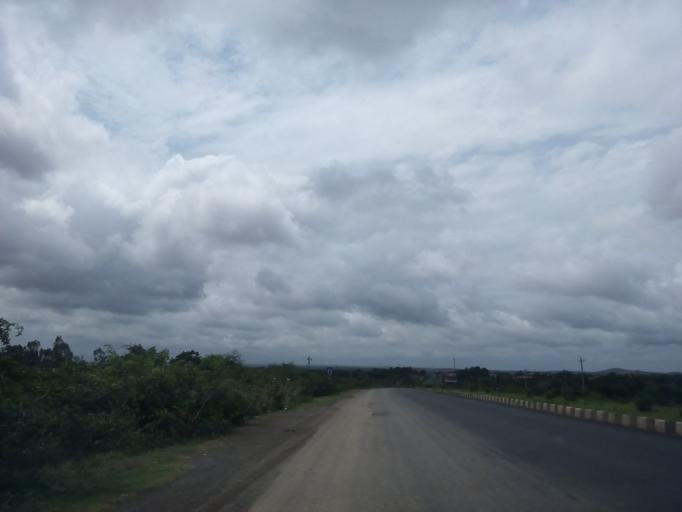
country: IN
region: Karnataka
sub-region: Haveri
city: Byadgi
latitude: 14.7021
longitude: 75.5217
